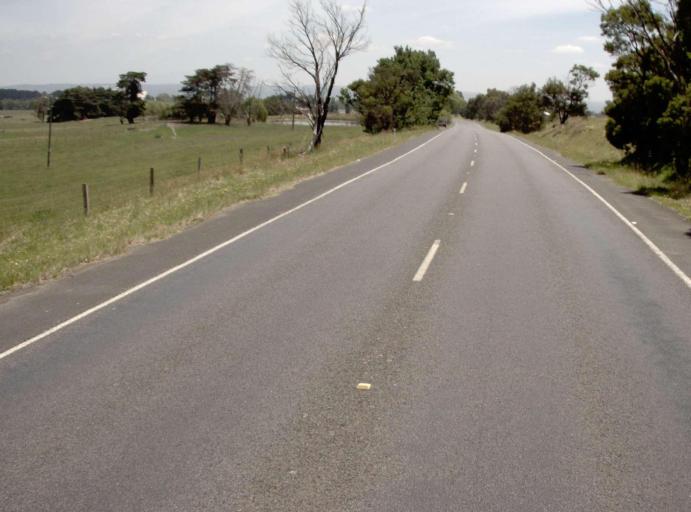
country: AU
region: Victoria
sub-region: Latrobe
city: Traralgon
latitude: -38.2173
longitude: 146.5469
